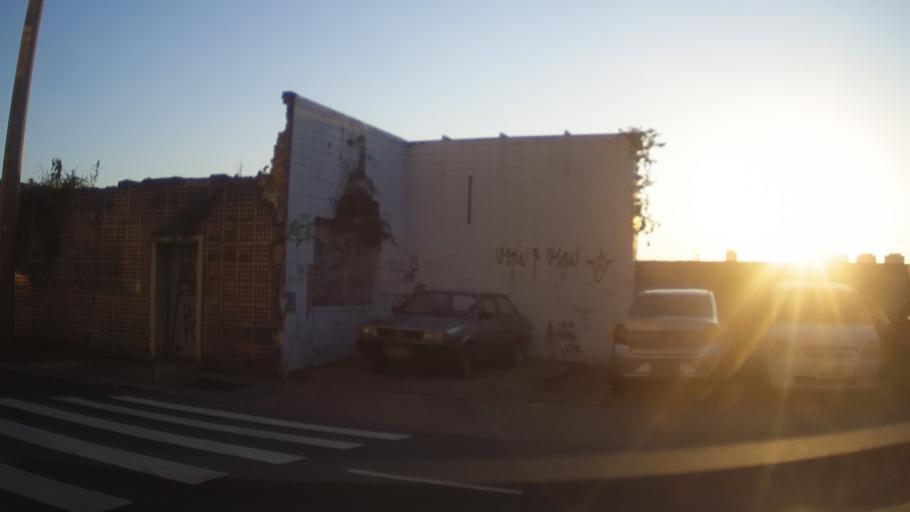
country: BR
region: Sao Paulo
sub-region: Sao Caetano Do Sul
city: Sao Caetano do Sul
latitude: -23.6162
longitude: -46.5766
